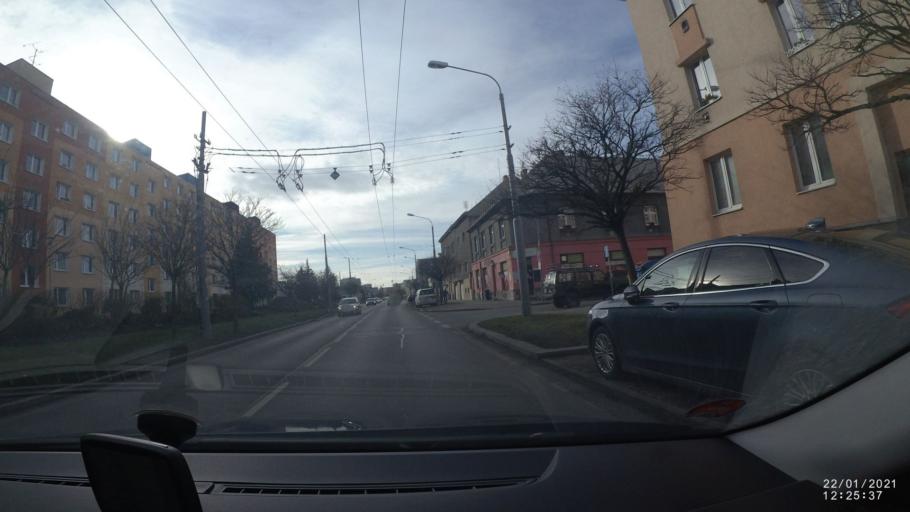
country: CZ
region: Plzensky
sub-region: Okres Plzen-Mesto
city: Pilsen
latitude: 49.7559
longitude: 13.4193
